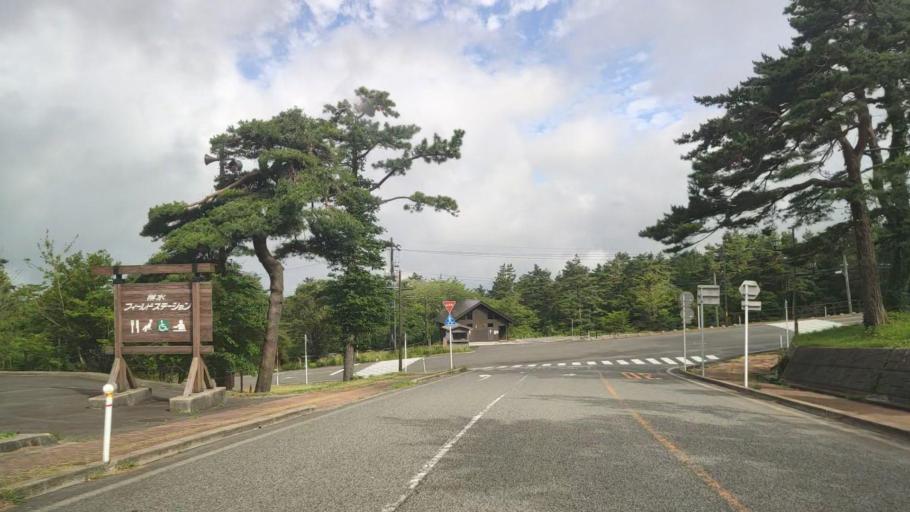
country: JP
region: Tottori
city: Yonago
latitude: 35.3685
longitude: 133.5142
